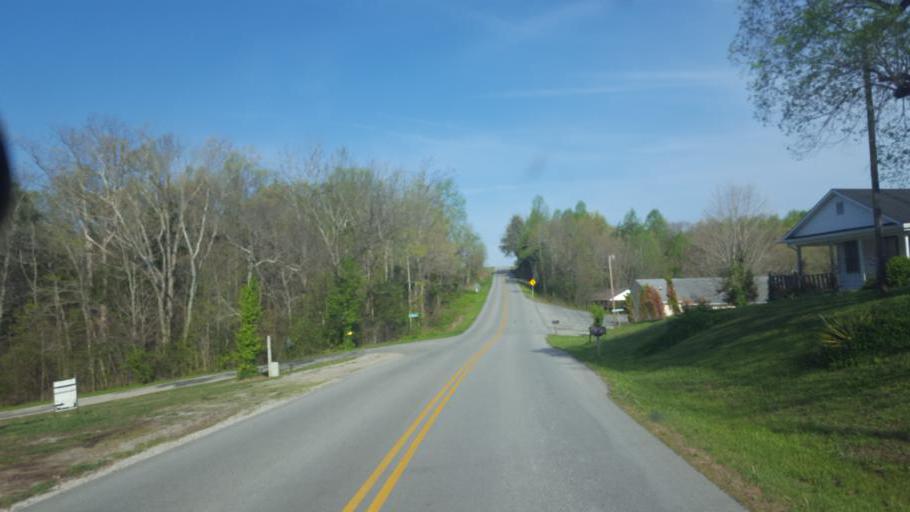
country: US
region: Kentucky
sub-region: Hart County
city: Munfordville
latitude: 37.3167
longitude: -86.0879
